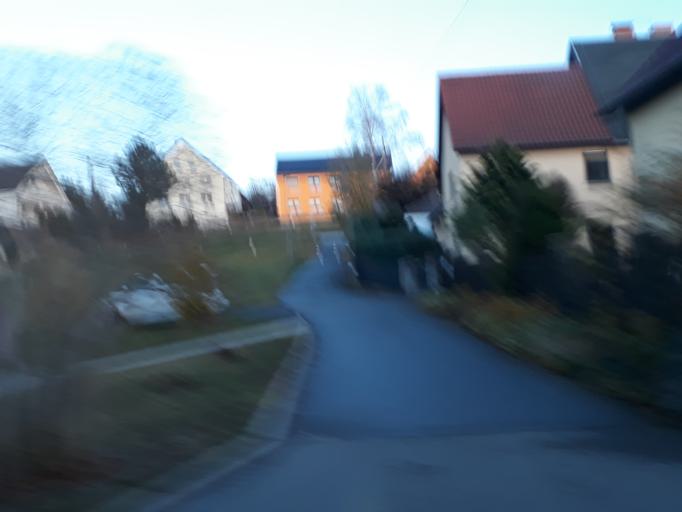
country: DE
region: Saxony
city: Reinhardtsgrimma
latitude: 50.9065
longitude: 13.7864
